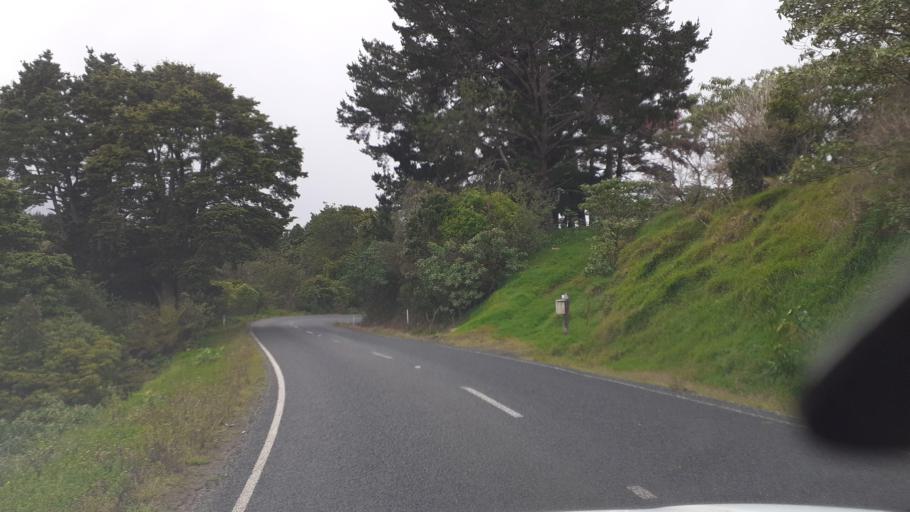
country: NZ
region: Northland
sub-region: Far North District
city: Waimate North
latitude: -35.4577
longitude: 173.7815
